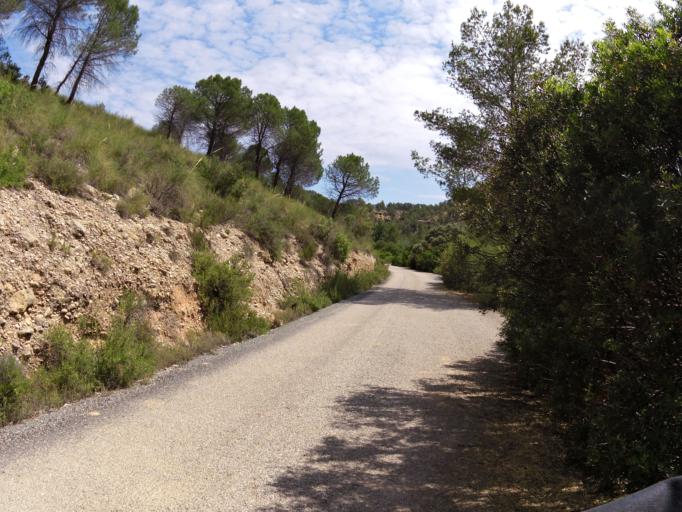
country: ES
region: Castille-La Mancha
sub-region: Provincia de Albacete
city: Casas Ibanez
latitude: 39.3664
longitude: -1.4500
